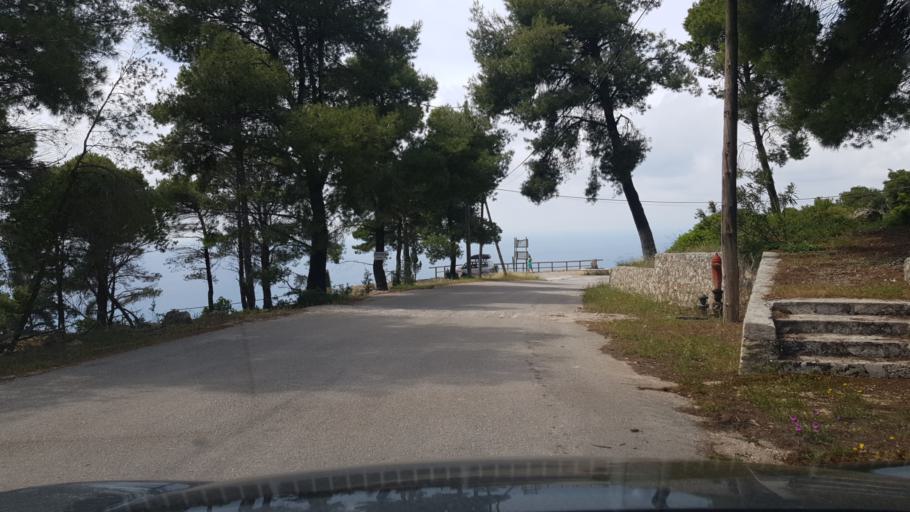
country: GR
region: Ionian Islands
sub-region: Lefkada
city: Nidri
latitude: 38.6280
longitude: 20.5623
